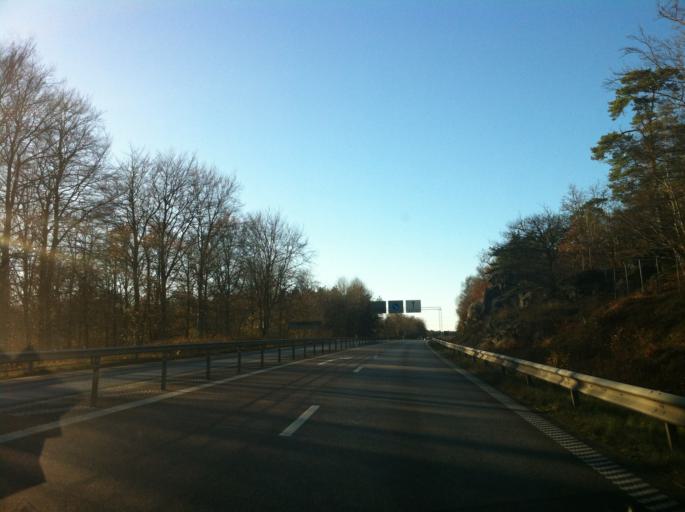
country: SE
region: Blekinge
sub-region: Karlshamns Kommun
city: Karlshamn
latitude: 56.1867
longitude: 14.8355
